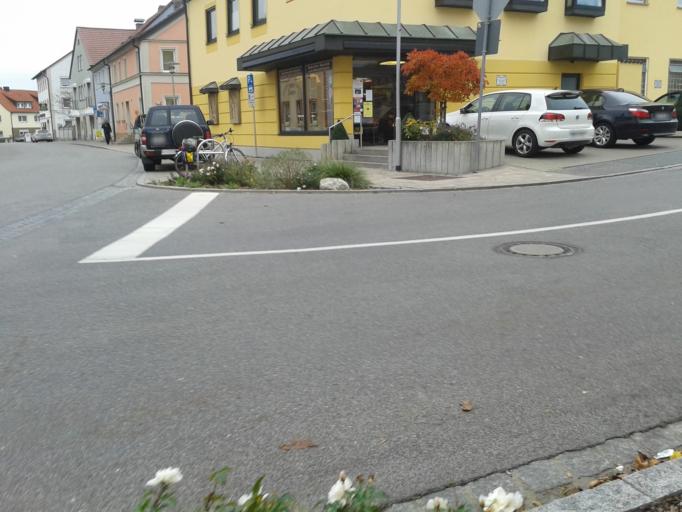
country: DE
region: Bavaria
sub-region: Upper Franconia
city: Memmelsdorf
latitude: 49.9326
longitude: 10.9546
